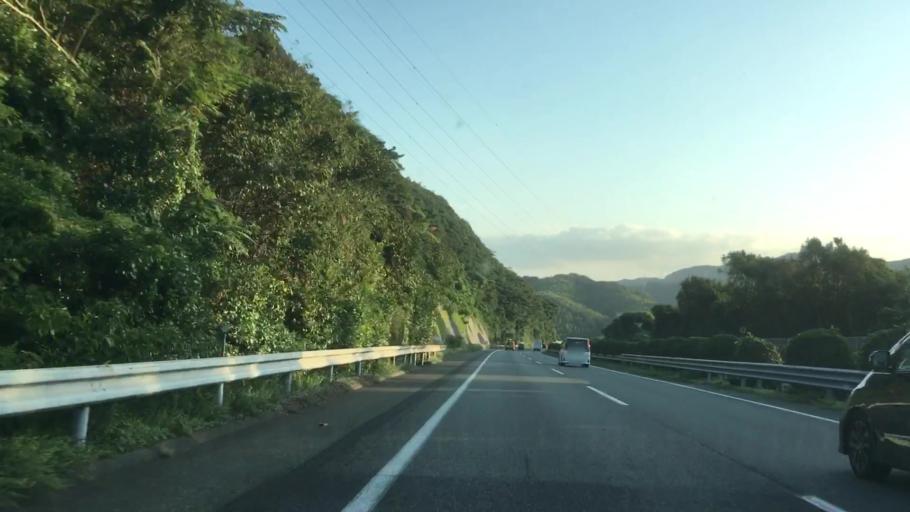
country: JP
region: Yamaguchi
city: Shimonoseki
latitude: 33.9131
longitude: 130.9759
